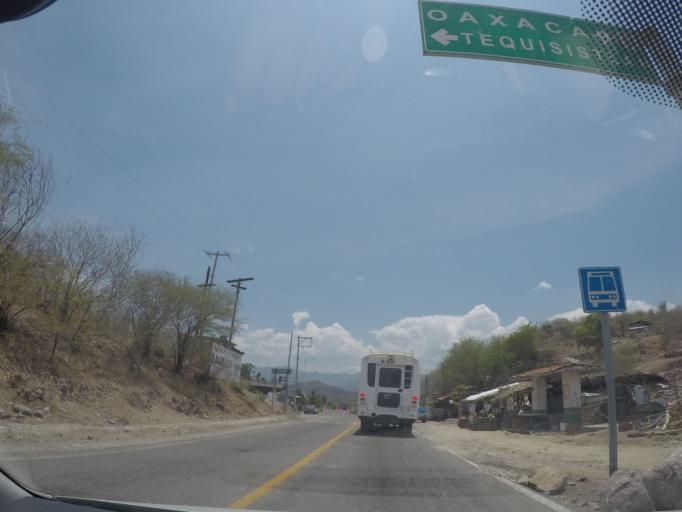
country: MX
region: Oaxaca
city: Magdalena Tequisistlan
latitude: 16.4127
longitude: -95.5947
